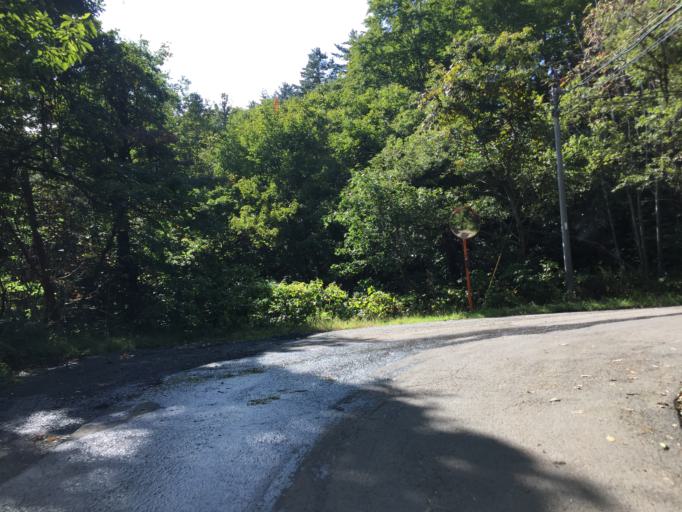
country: JP
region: Yamagata
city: Yonezawa
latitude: 37.8116
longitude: 140.2674
